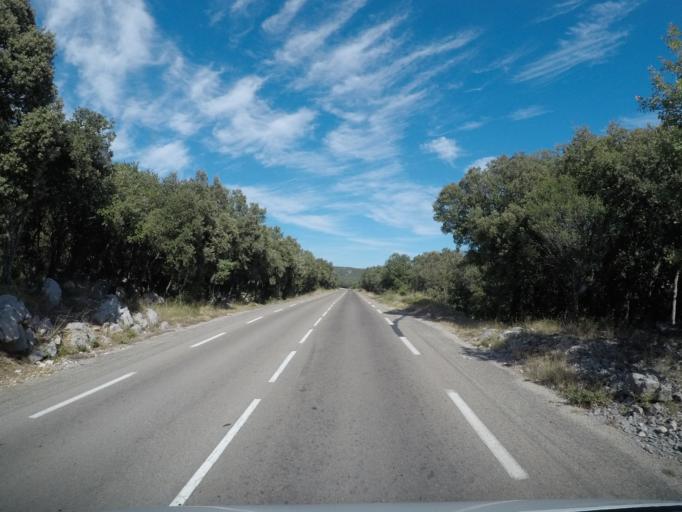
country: FR
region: Languedoc-Roussillon
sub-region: Departement du Gard
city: Sauve
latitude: 43.9667
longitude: 3.9199
